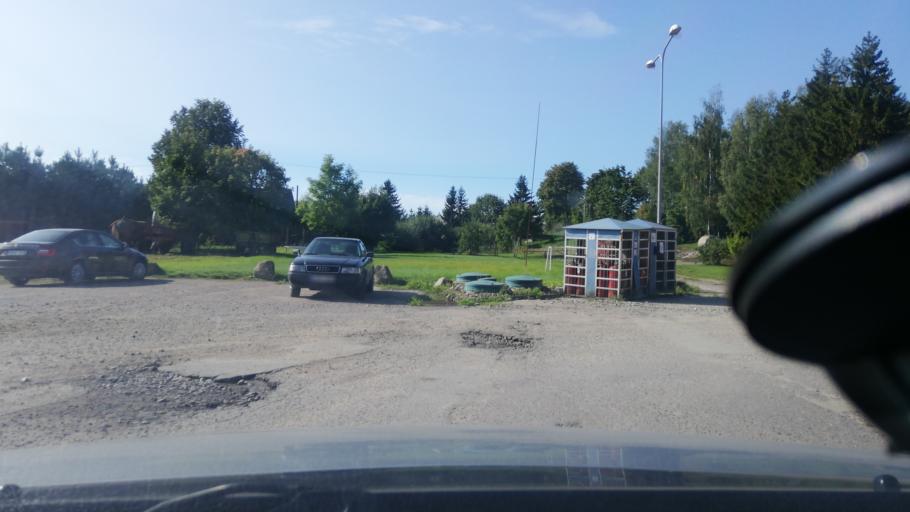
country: LT
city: Salantai
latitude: 55.9169
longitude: 21.4678
